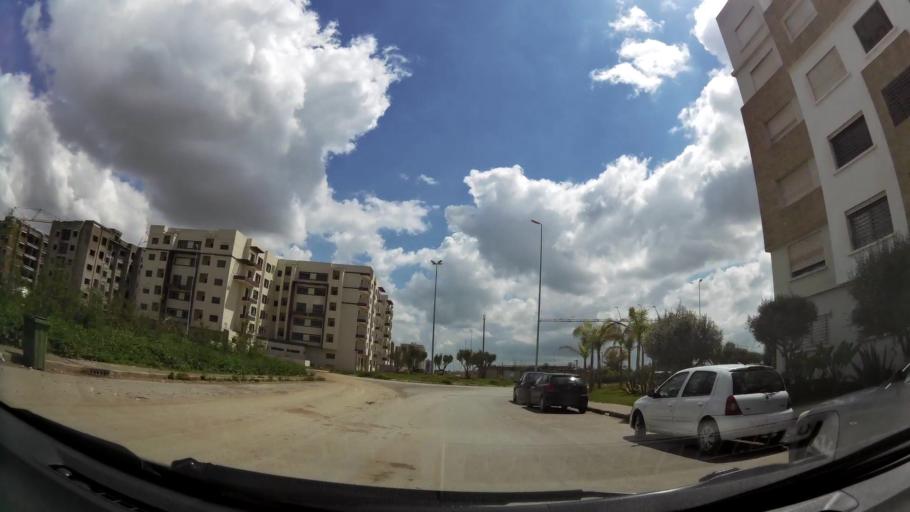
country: MA
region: Chaouia-Ouardigha
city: Nouaseur
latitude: 33.3915
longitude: -7.5615
